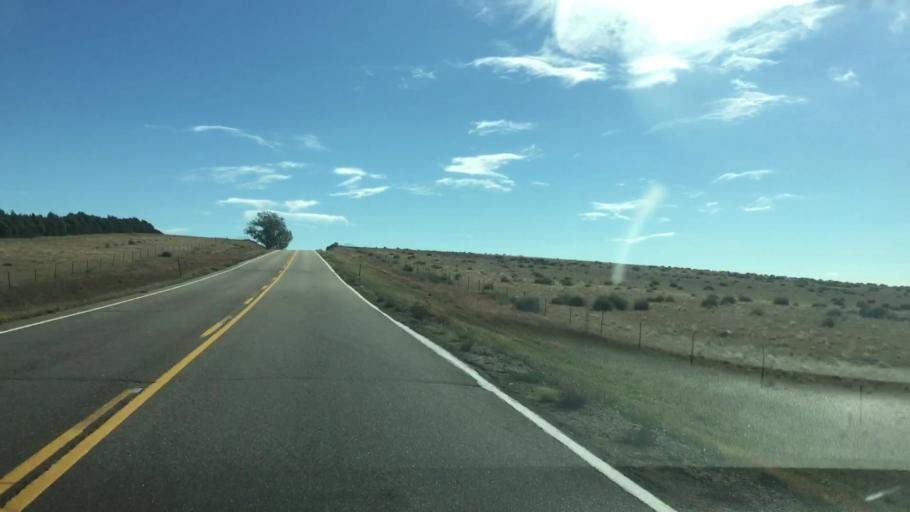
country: US
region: Colorado
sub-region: Elbert County
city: Kiowa
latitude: 39.2736
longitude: -104.2134
